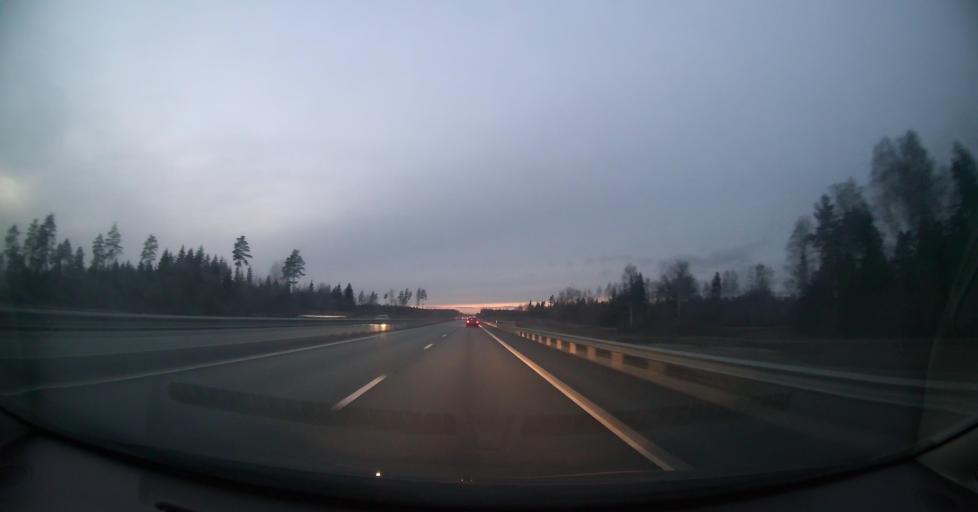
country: EE
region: Harju
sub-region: Anija vald
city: Kehra
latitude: 59.1498
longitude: 25.2285
